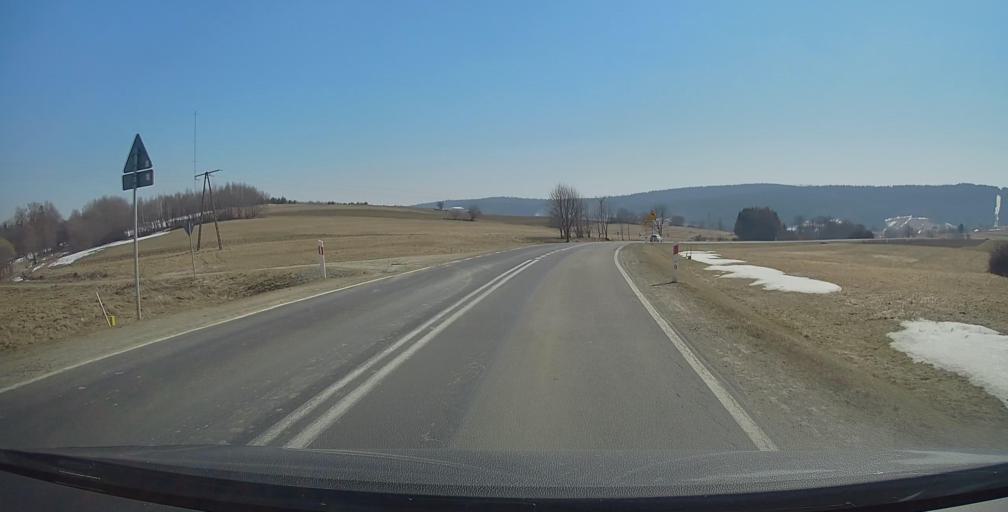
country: PL
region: Subcarpathian Voivodeship
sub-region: Powiat sanocki
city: Tyrawa Woloska
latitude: 49.6281
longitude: 22.4295
